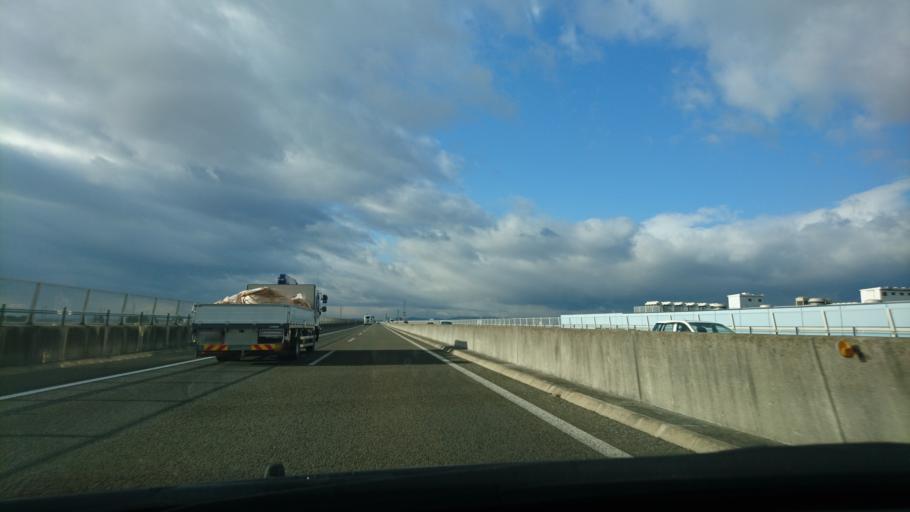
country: JP
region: Miyagi
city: Rifu
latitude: 38.2599
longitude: 140.9670
